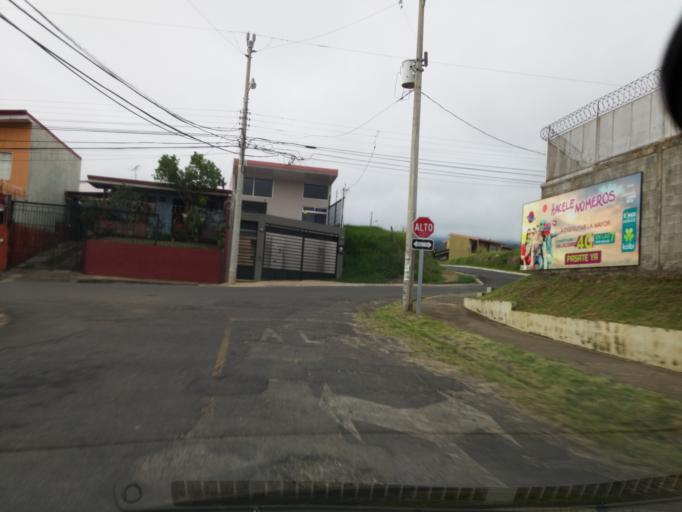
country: CR
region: Heredia
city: San Rafael
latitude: 10.0131
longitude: -84.1092
